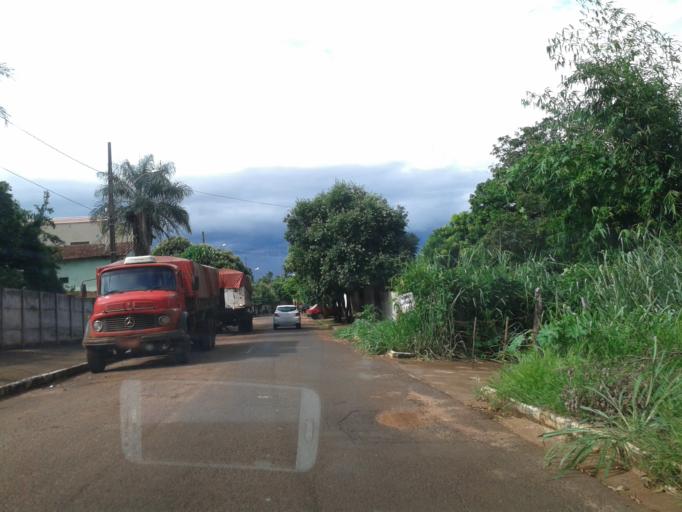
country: BR
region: Minas Gerais
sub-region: Ituiutaba
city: Ituiutaba
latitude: -18.9828
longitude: -49.4746
